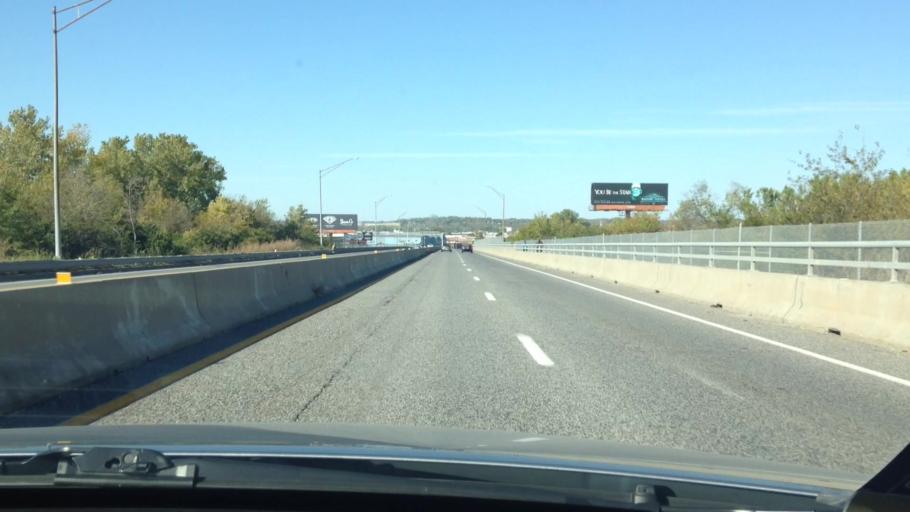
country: US
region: Missouri
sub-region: Clay County
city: North Kansas City
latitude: 39.1201
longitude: -94.5795
